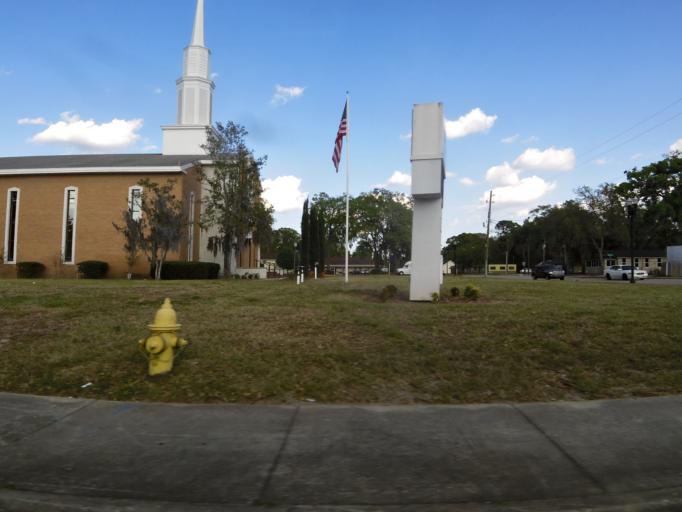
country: US
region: Florida
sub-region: Duval County
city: Jacksonville
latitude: 30.3338
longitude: -81.5969
